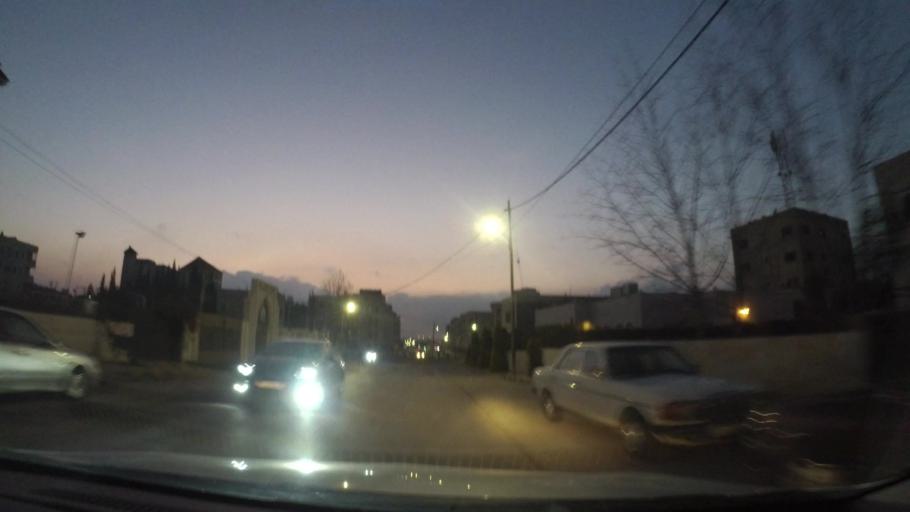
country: JO
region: Amman
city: Al Bunayyat ash Shamaliyah
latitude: 31.8947
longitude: 35.9214
